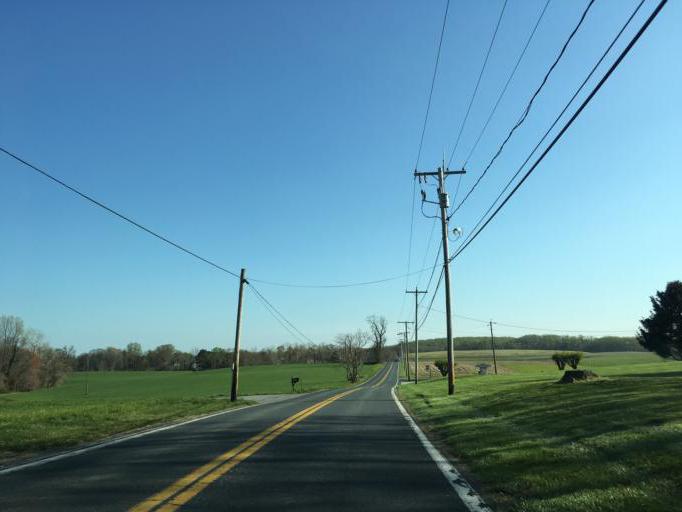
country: US
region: Maryland
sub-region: Baltimore County
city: Perry Hall
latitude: 39.4486
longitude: -76.4957
